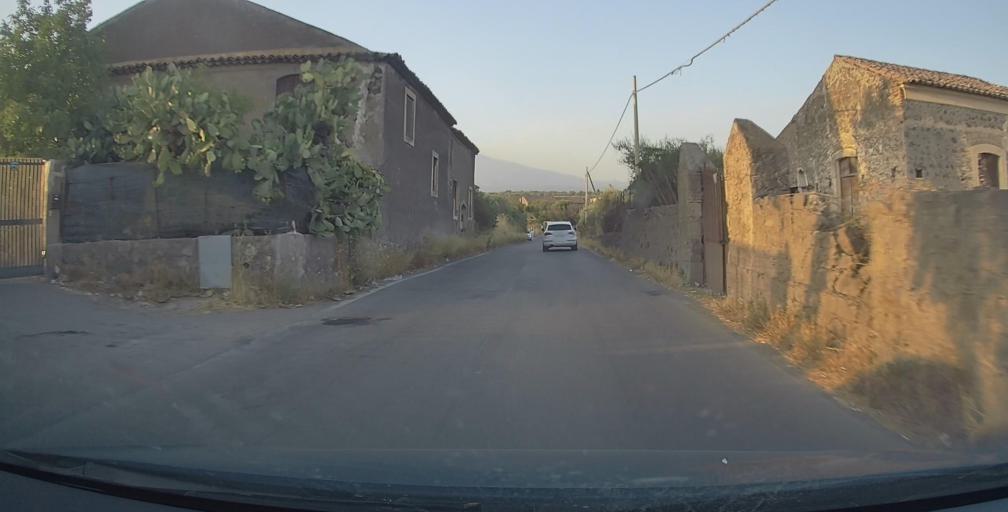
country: IT
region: Sicily
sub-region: Catania
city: Palazzolo
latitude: 37.5474
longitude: 14.9324
